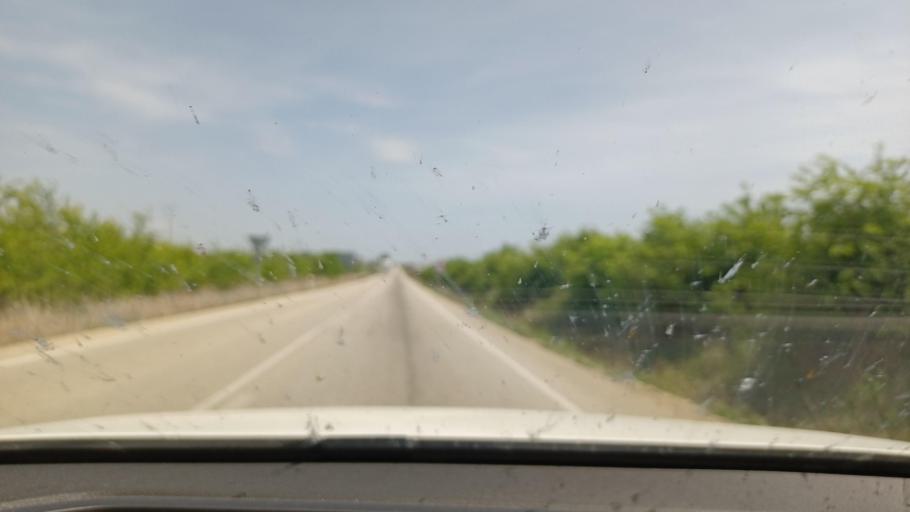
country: ES
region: Castille and Leon
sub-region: Provincia de Soria
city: Almazan
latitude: 41.4760
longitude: -2.5187
